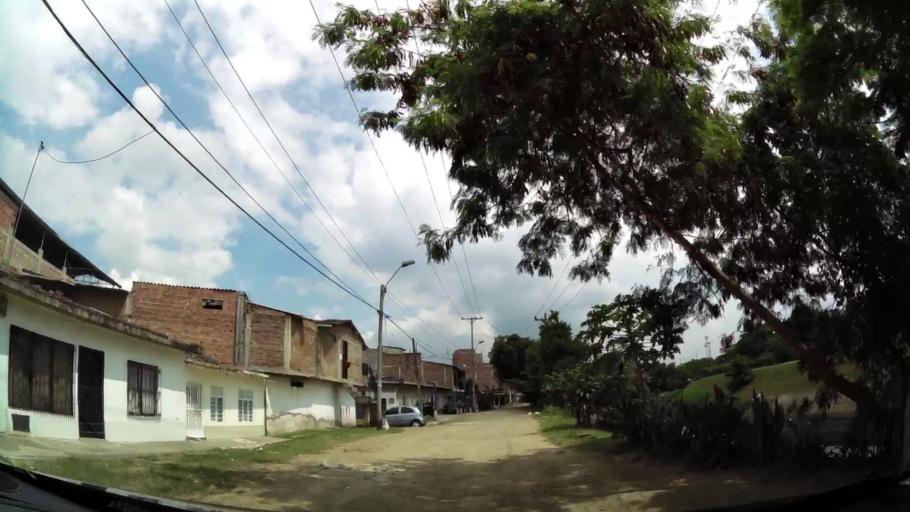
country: CO
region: Valle del Cauca
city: Cali
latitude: 3.4897
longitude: -76.4863
